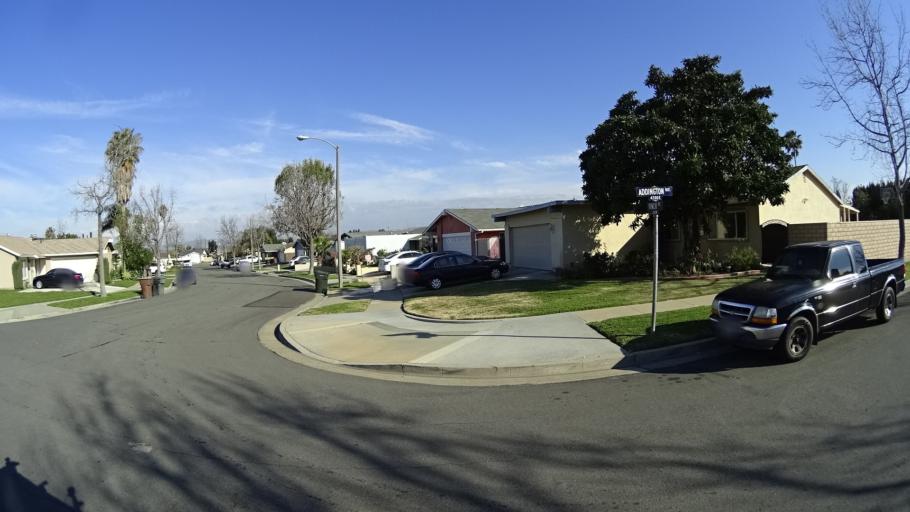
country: US
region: California
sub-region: Orange County
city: Villa Park
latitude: 33.8460
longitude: -117.8267
